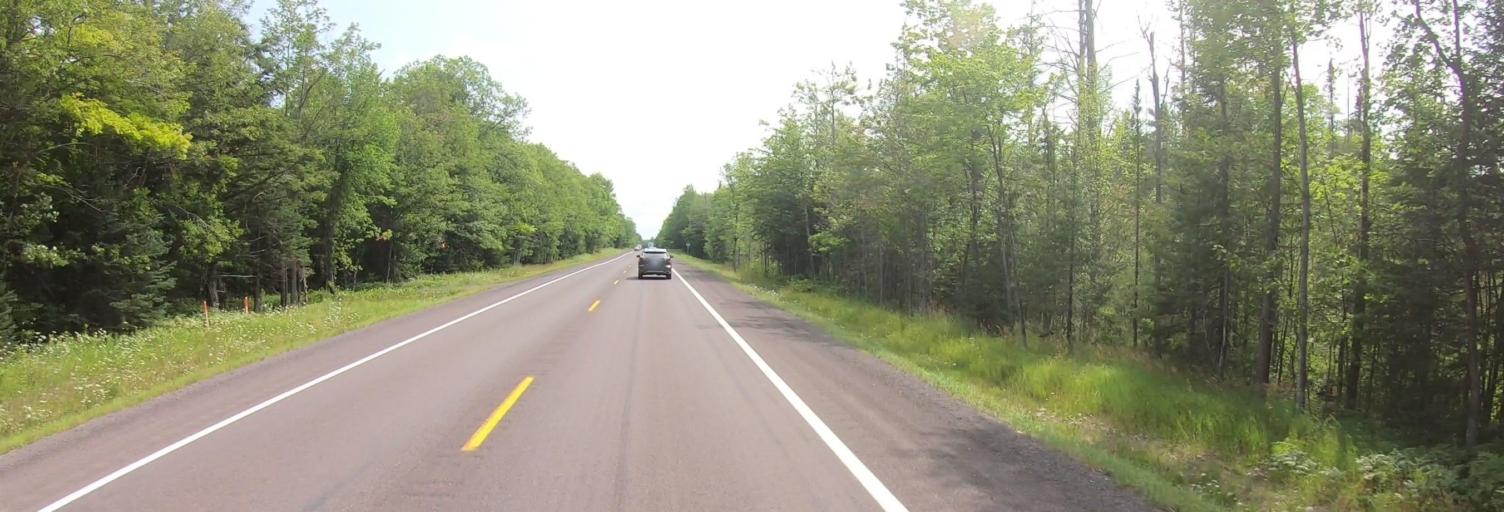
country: US
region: Michigan
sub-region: Houghton County
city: Hancock
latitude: 46.9822
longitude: -88.7810
